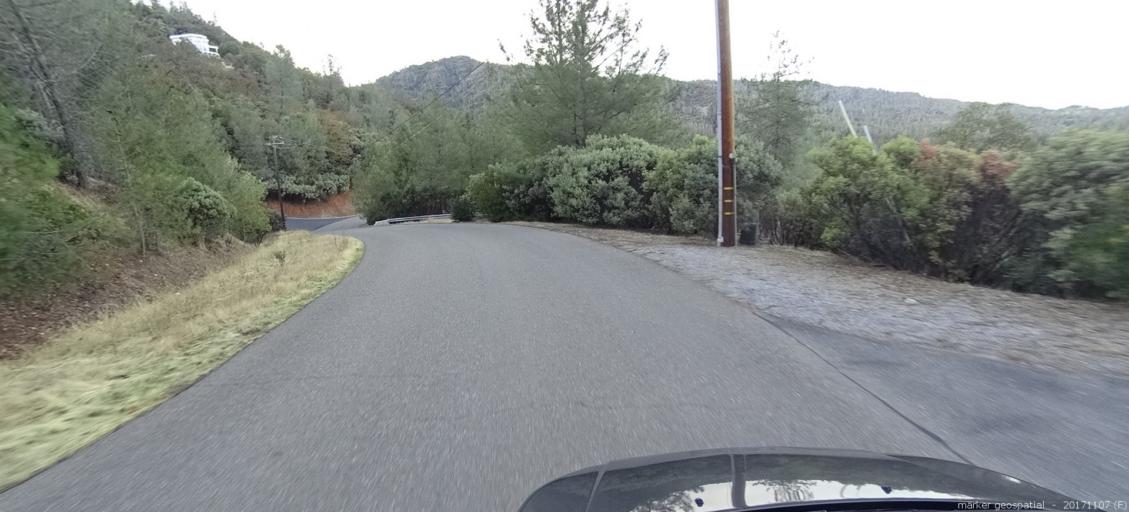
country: US
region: California
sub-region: Shasta County
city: Shasta
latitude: 40.5433
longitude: -122.5007
